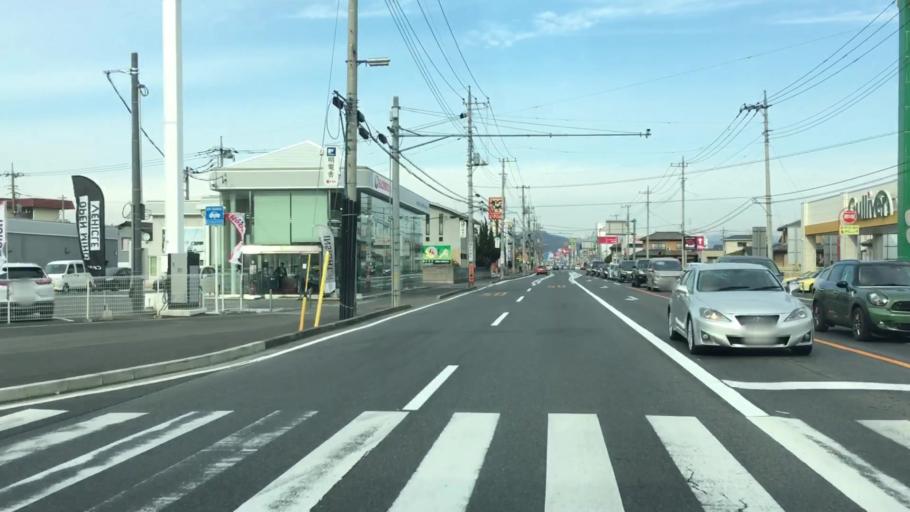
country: JP
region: Gunma
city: Ota
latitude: 36.2695
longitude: 139.3771
